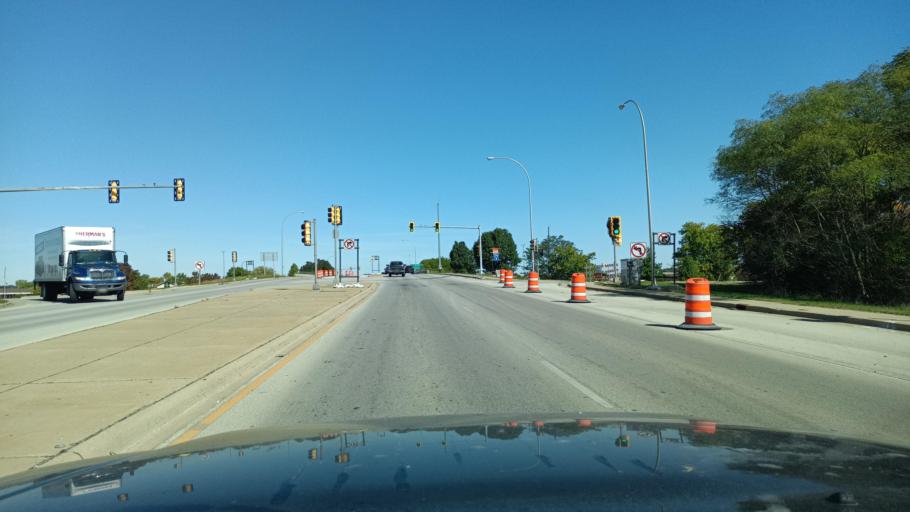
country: US
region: Illinois
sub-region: Champaign County
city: Champaign
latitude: 40.1331
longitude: -88.2436
